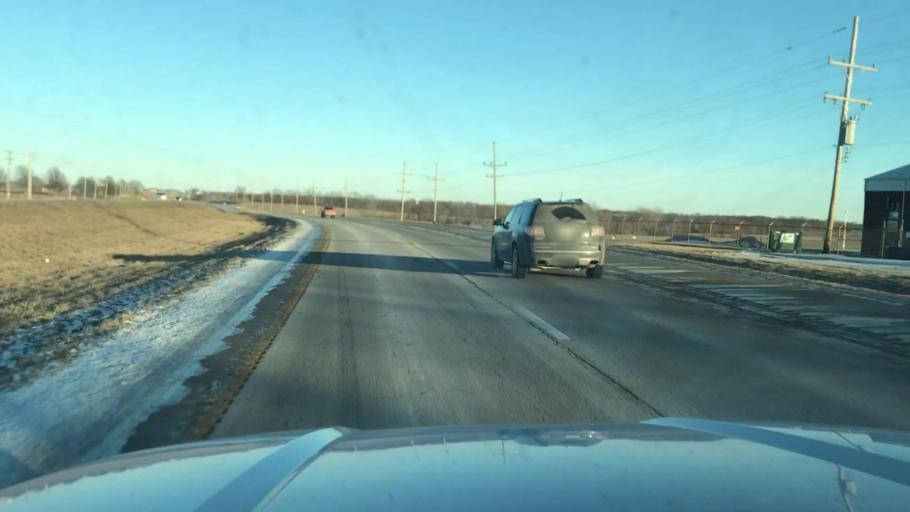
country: US
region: Missouri
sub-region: Clinton County
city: Cameron
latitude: 39.7547
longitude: -94.3374
